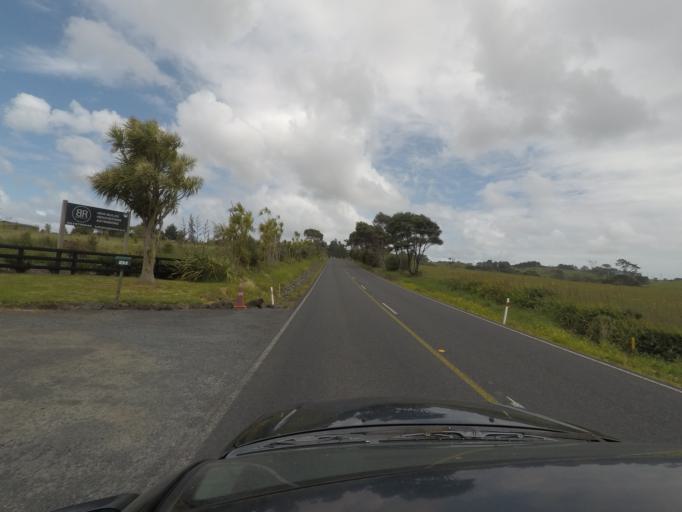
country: NZ
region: Auckland
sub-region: Auckland
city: Parakai
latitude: -36.6332
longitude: 174.5044
